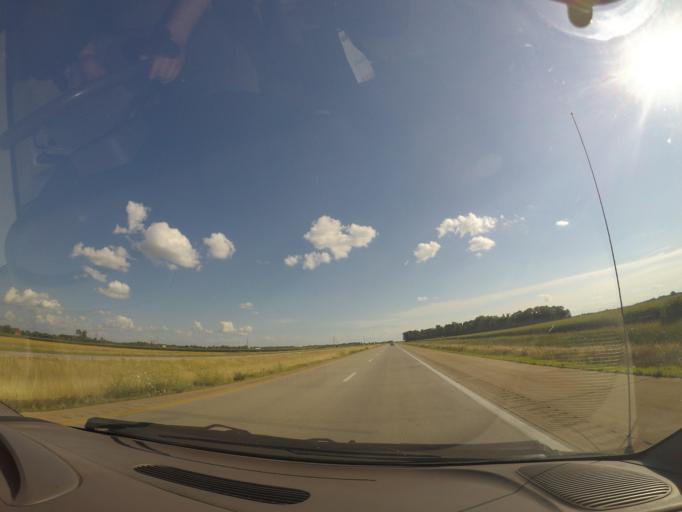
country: US
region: Ohio
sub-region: Lucas County
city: Whitehouse
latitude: 41.4870
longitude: -83.7718
